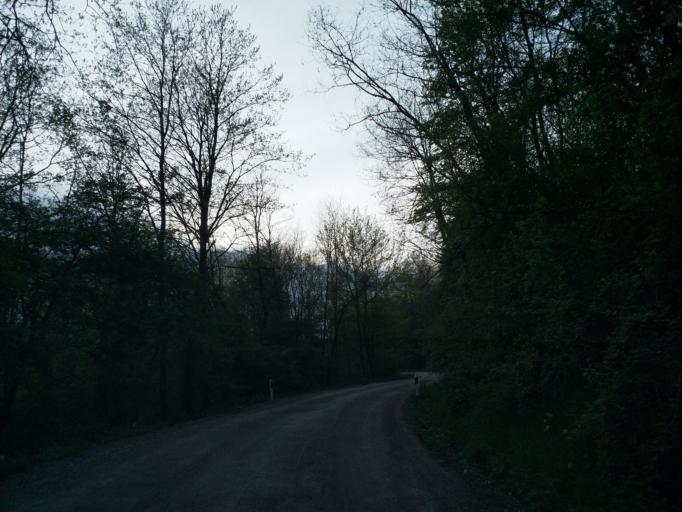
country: RS
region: Central Serbia
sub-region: Pomoravski Okrug
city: Despotovac
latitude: 43.9560
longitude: 21.5690
